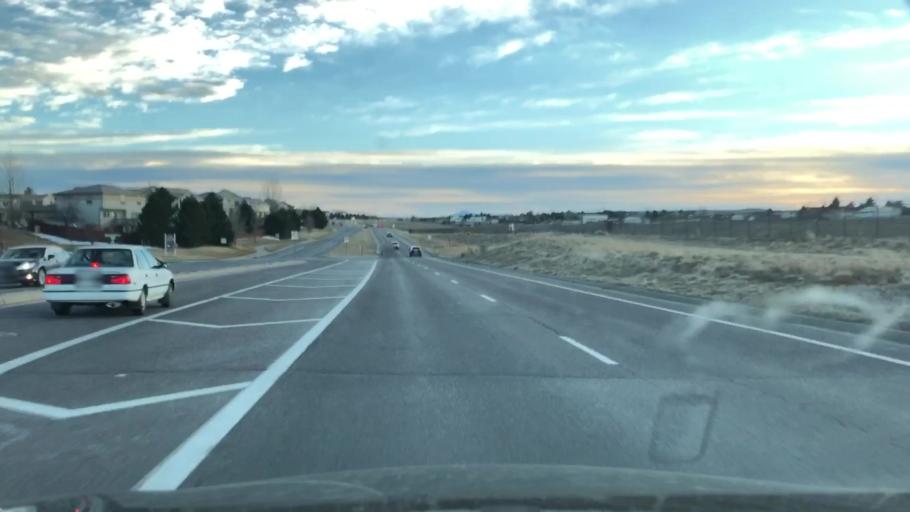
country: US
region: Colorado
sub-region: Douglas County
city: Stonegate
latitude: 39.5495
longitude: -104.8090
